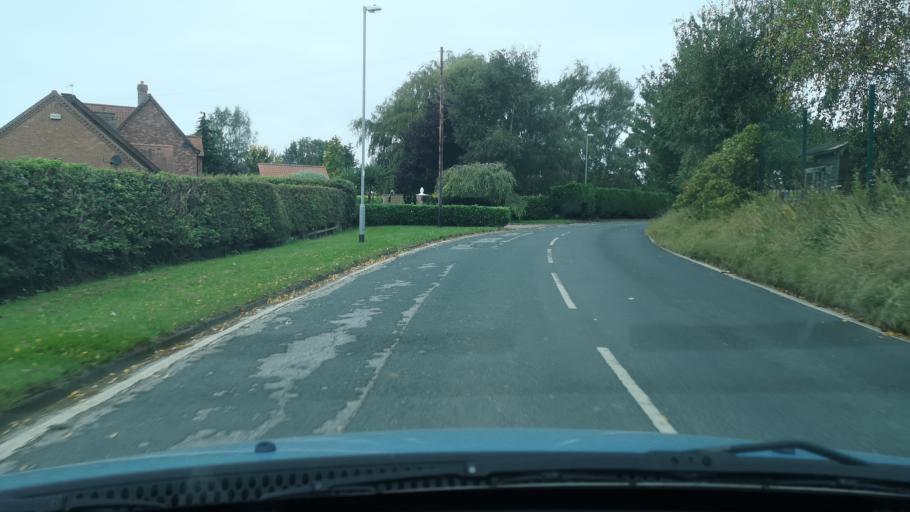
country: GB
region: England
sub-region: East Riding of Yorkshire
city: Laxton
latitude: 53.6951
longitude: -0.7832
